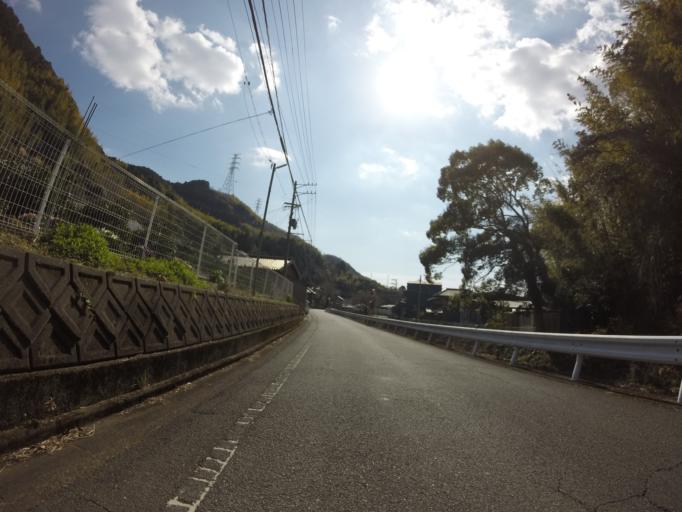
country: JP
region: Shizuoka
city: Shizuoka-shi
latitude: 35.0718
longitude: 138.4843
